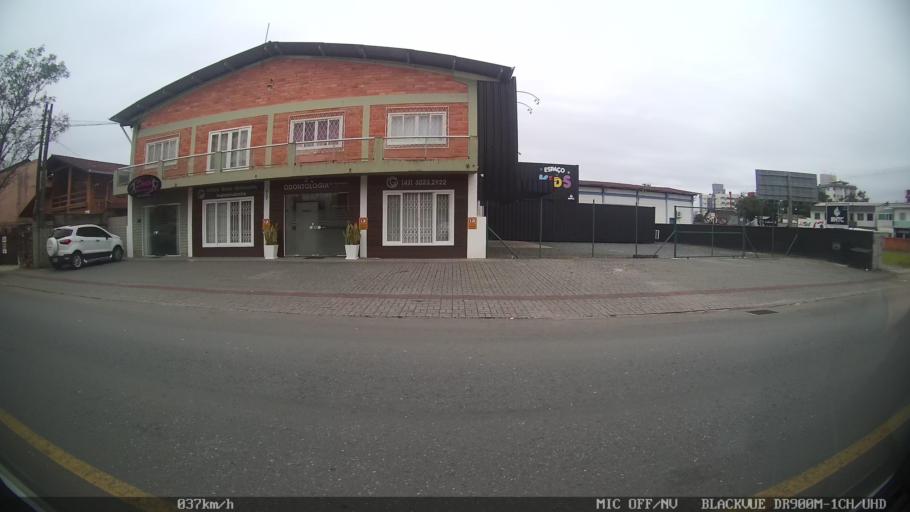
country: BR
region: Santa Catarina
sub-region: Joinville
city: Joinville
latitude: -26.2765
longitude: -48.8464
